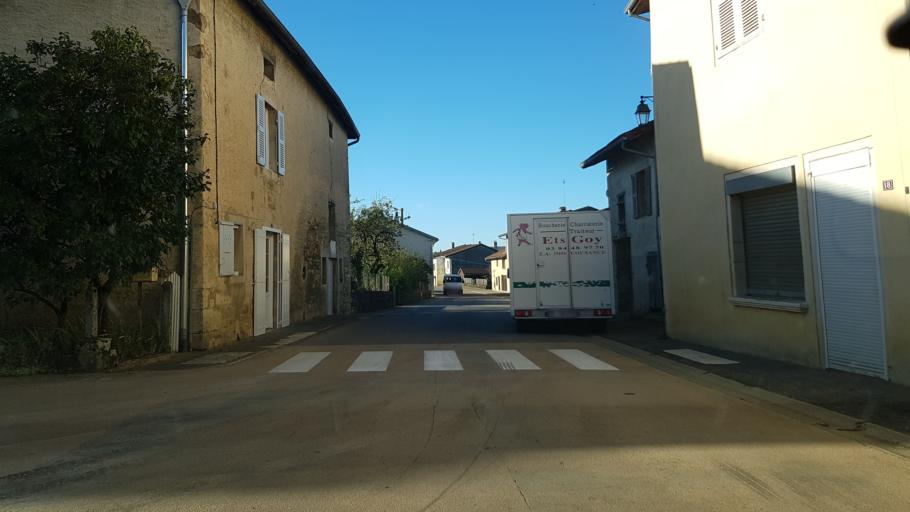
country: FR
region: Bourgogne
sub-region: Departement de Saone-et-Loire
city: Cuiseaux
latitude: 46.4517
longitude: 5.4600
